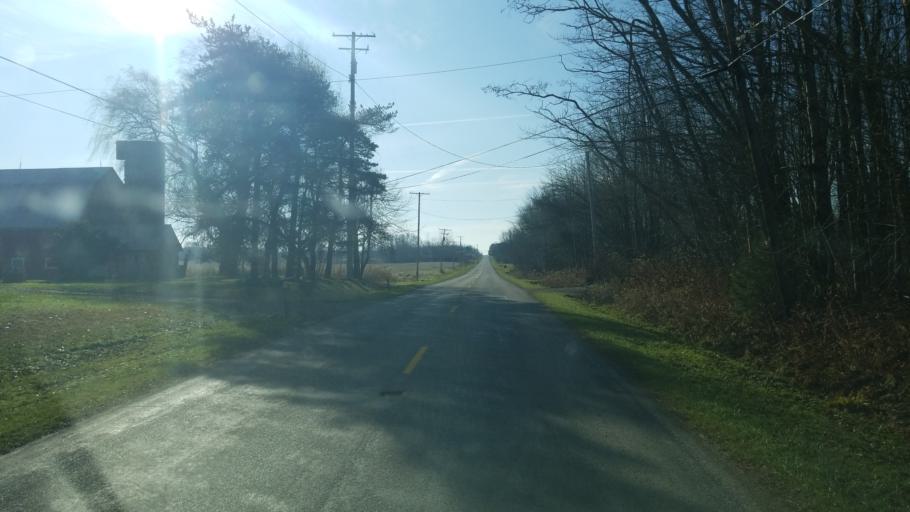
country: US
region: Ohio
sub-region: Ashtabula County
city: Jefferson
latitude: 41.8066
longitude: -80.7132
